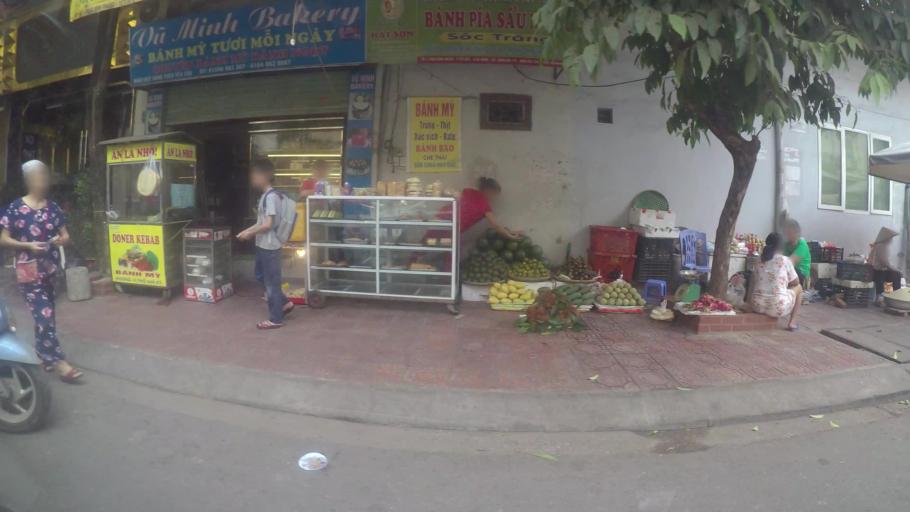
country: VN
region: Ha Noi
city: Ha Dong
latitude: 20.9722
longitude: 105.7758
